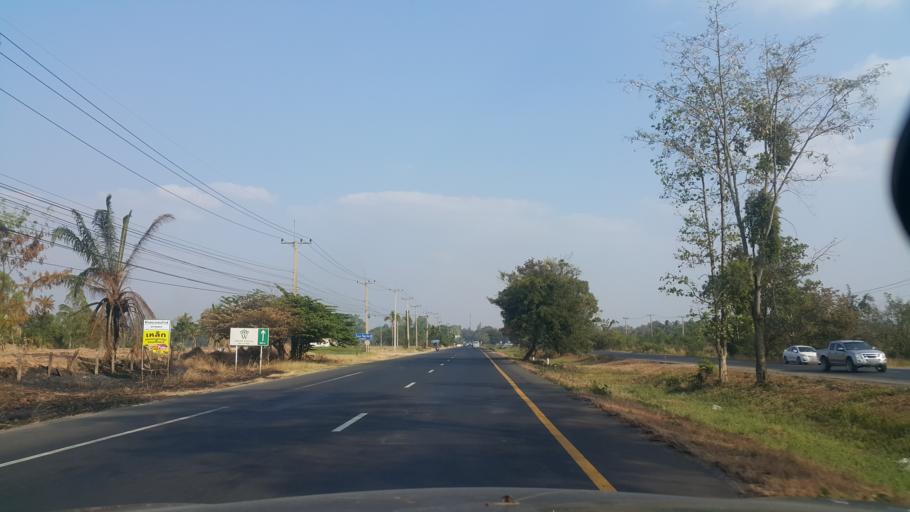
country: TH
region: Buriram
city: Nang Rong
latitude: 14.6350
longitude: 102.7124
